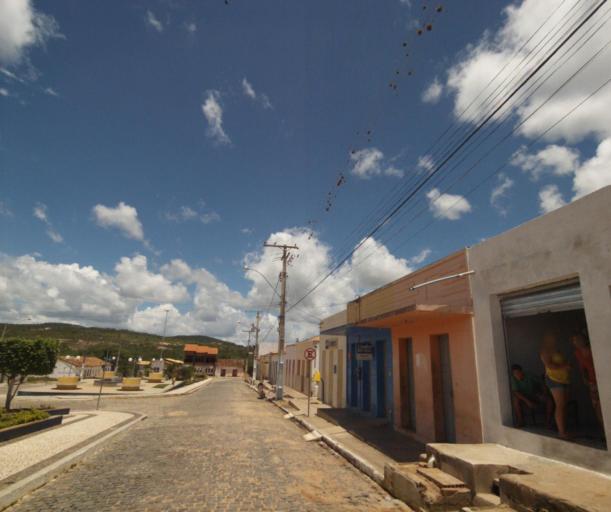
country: BR
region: Bahia
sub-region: Pocoes
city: Pocoes
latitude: -14.3755
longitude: -40.5047
